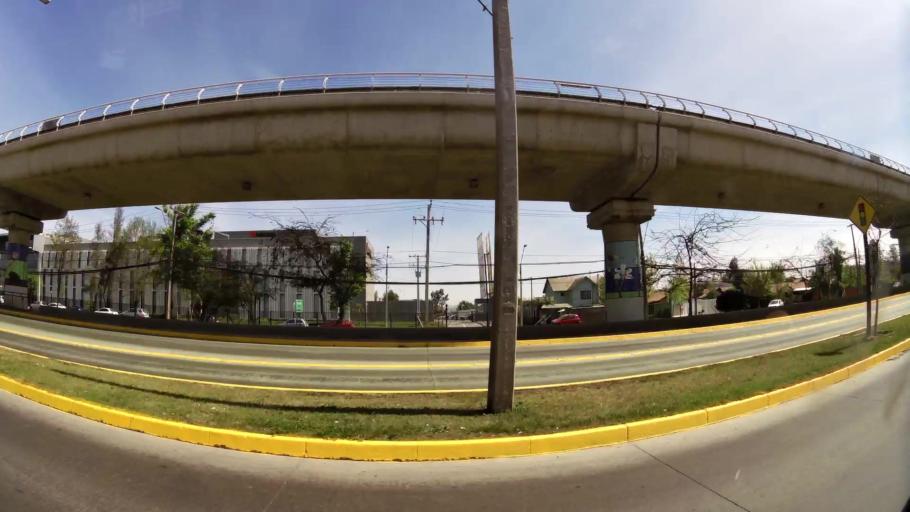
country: CL
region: Santiago Metropolitan
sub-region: Provincia de Cordillera
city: Puente Alto
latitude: -33.5847
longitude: -70.5806
